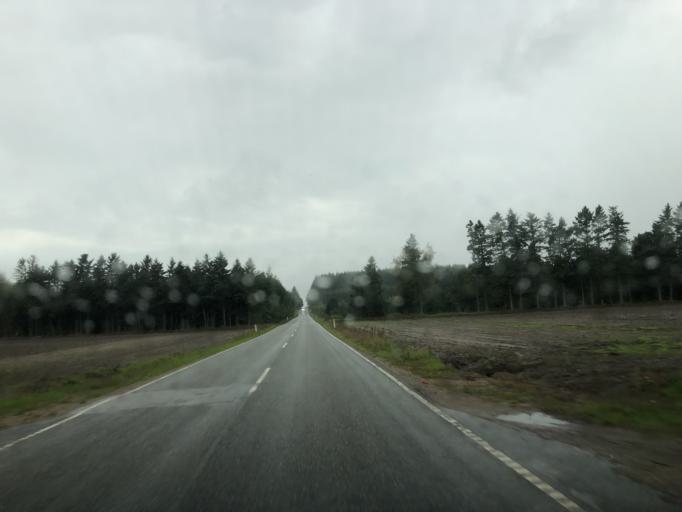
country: DK
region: Central Jutland
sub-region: Ikast-Brande Kommune
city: Brande
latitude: 55.9854
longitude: 9.2524
